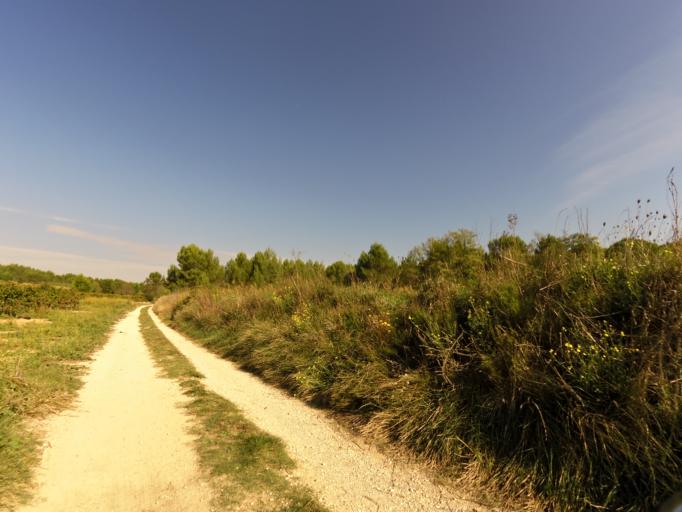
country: FR
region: Languedoc-Roussillon
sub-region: Departement du Gard
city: Aigues-Vives
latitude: 43.7525
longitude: 4.1883
